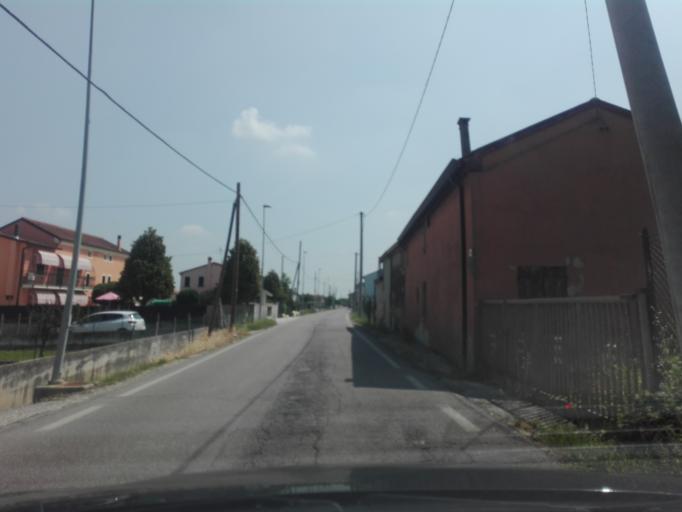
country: IT
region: Veneto
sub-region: Provincia di Rovigo
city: Lama Pezzoli
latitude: 45.0416
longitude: 11.9212
